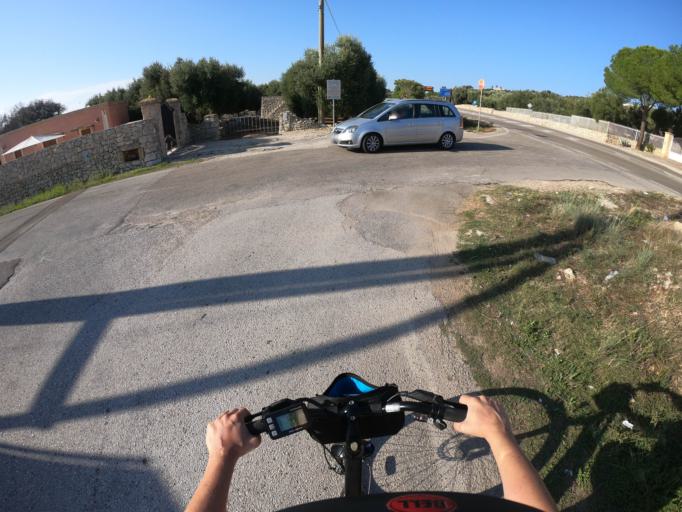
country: IT
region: Apulia
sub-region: Provincia di Lecce
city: Leuca
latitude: 39.8082
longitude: 18.3657
